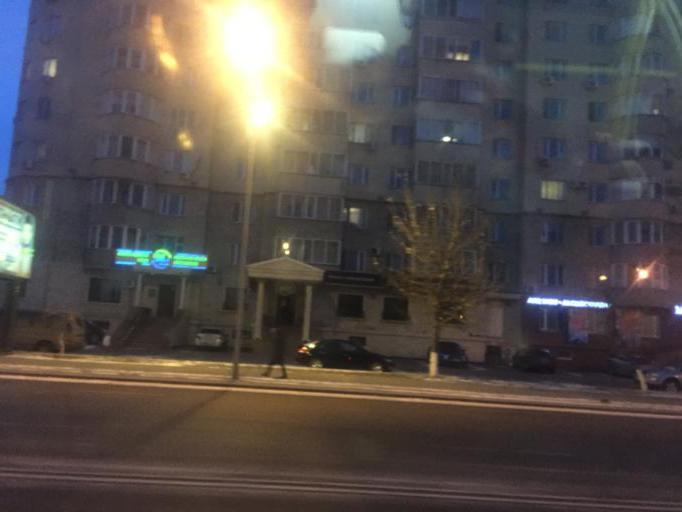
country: KZ
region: Astana Qalasy
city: Astana
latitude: 51.1734
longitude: 71.4117
